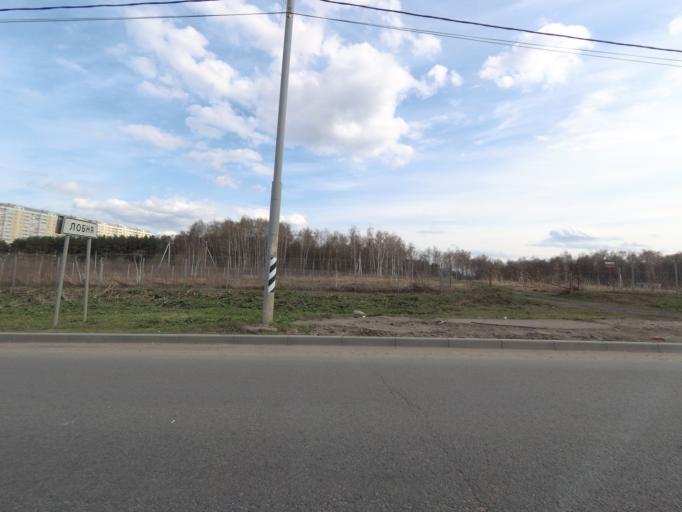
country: RU
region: Moskovskaya
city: Lobnya
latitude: 56.0030
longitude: 37.4275
